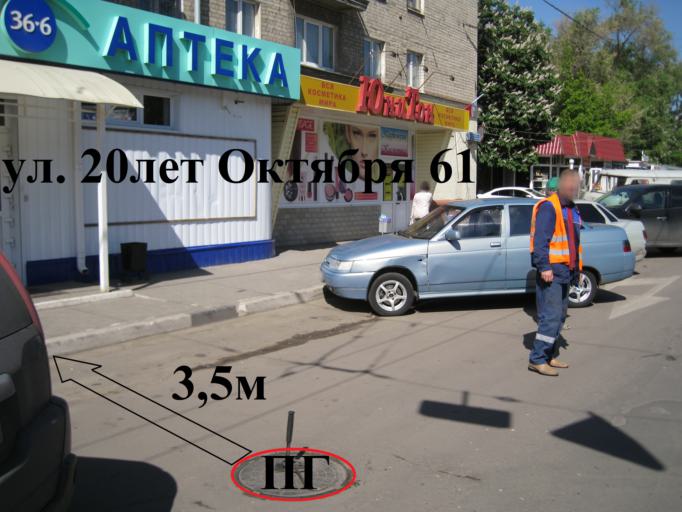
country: RU
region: Voronezj
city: Voronezh
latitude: 51.6463
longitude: 39.1976
